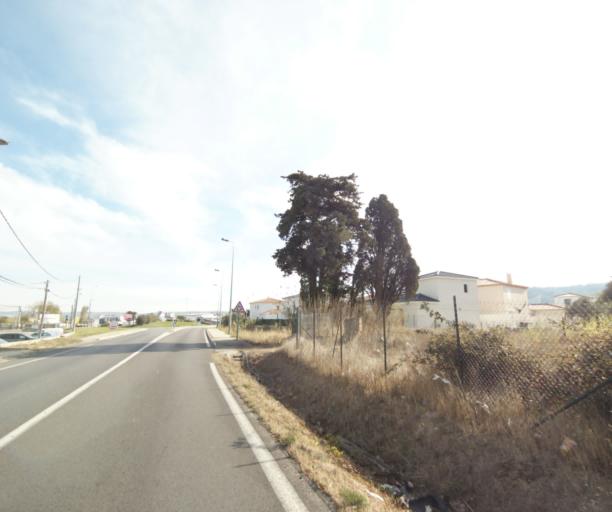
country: FR
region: Provence-Alpes-Cote d'Azur
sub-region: Departement des Bouches-du-Rhone
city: Chateauneuf-les-Martigues
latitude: 43.3908
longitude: 5.1608
